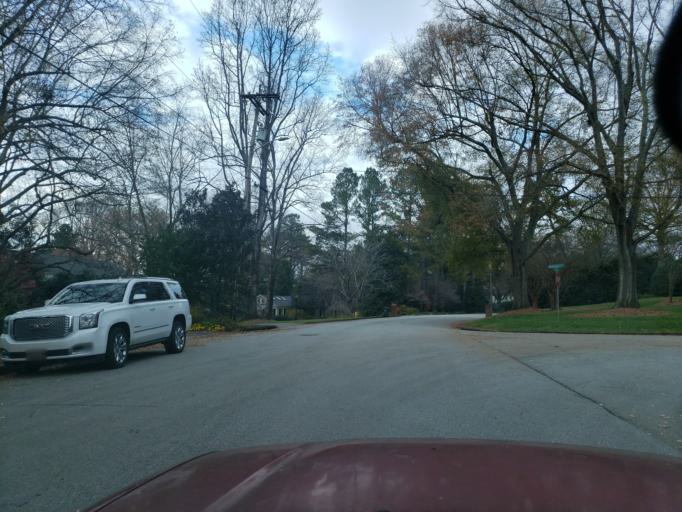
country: US
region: South Carolina
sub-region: Greenville County
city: Greenville
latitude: 34.8081
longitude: -82.3642
